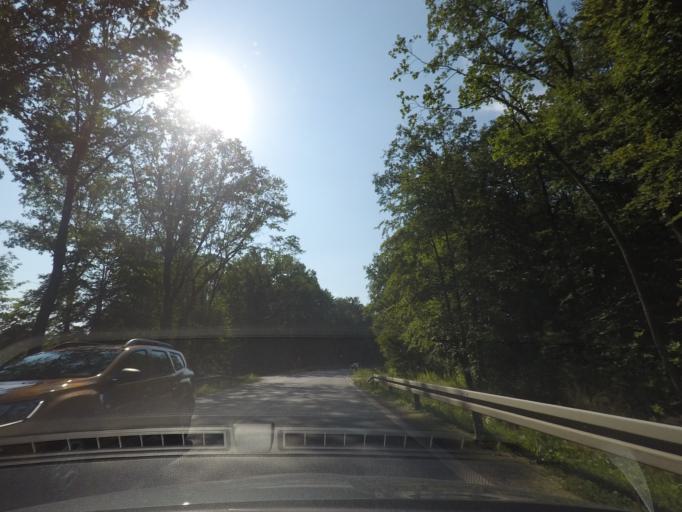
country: PL
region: Silesian Voivodeship
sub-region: Powiat pszczynski
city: Kryry
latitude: 50.0270
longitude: 18.8059
